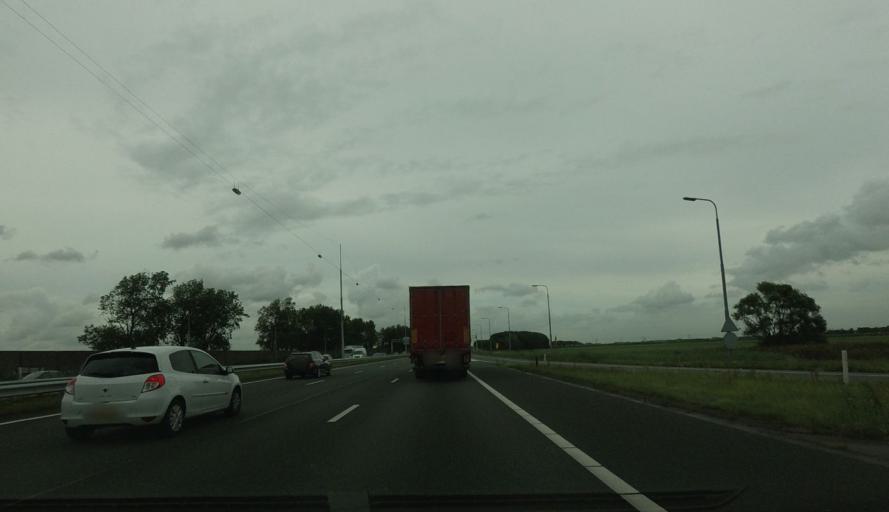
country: NL
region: North Holland
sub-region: Gemeente Uitgeest
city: Uitgeest
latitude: 52.5097
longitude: 4.7084
